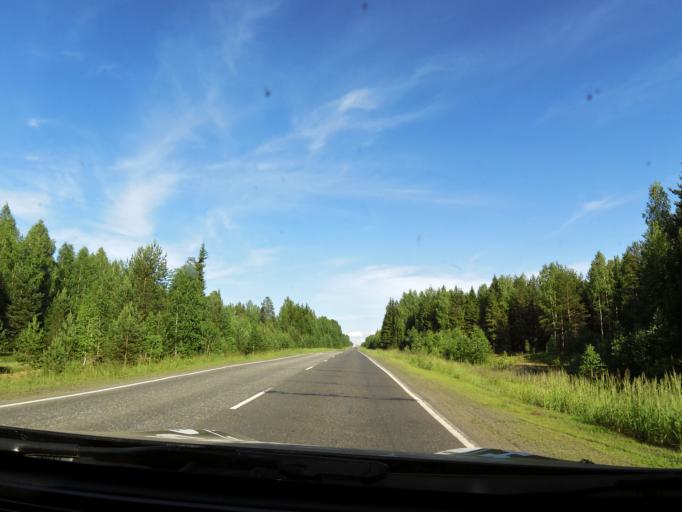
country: RU
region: Kirov
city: Chernaya Kholunitsa
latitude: 58.8874
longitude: 51.3806
